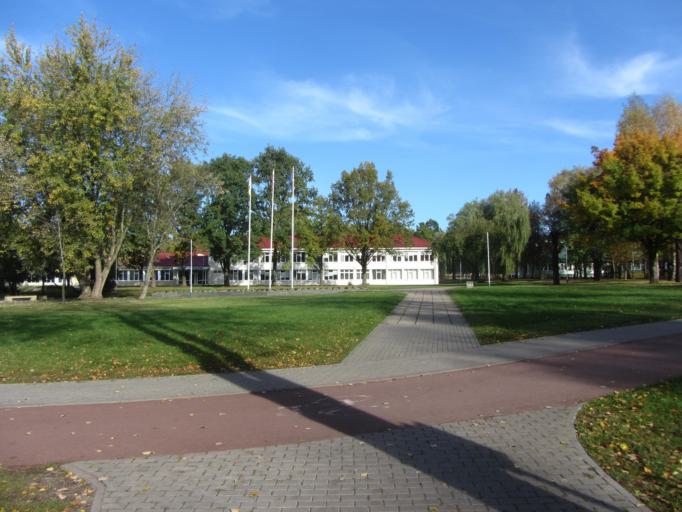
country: LT
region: Vilnius County
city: Elektrenai
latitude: 54.7834
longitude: 24.6604
